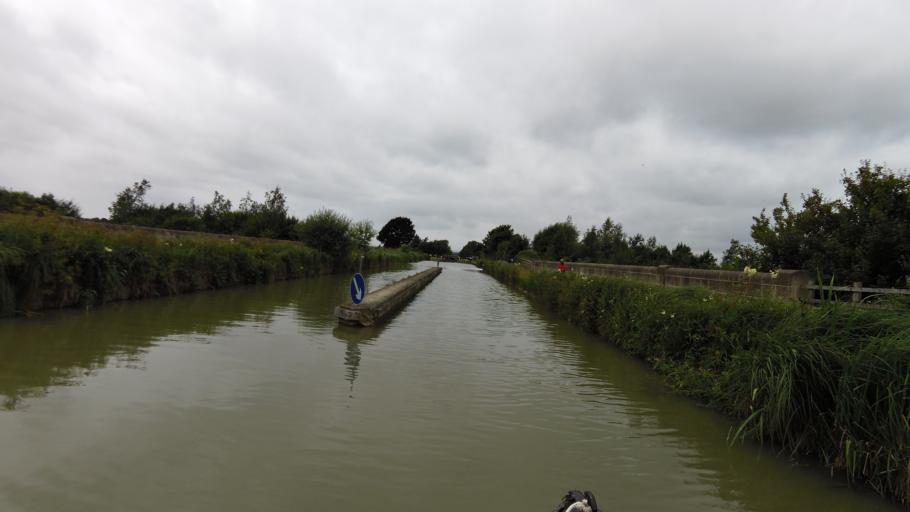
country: GB
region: England
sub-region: Wiltshire
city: Melksham
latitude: 51.3472
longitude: -2.1380
